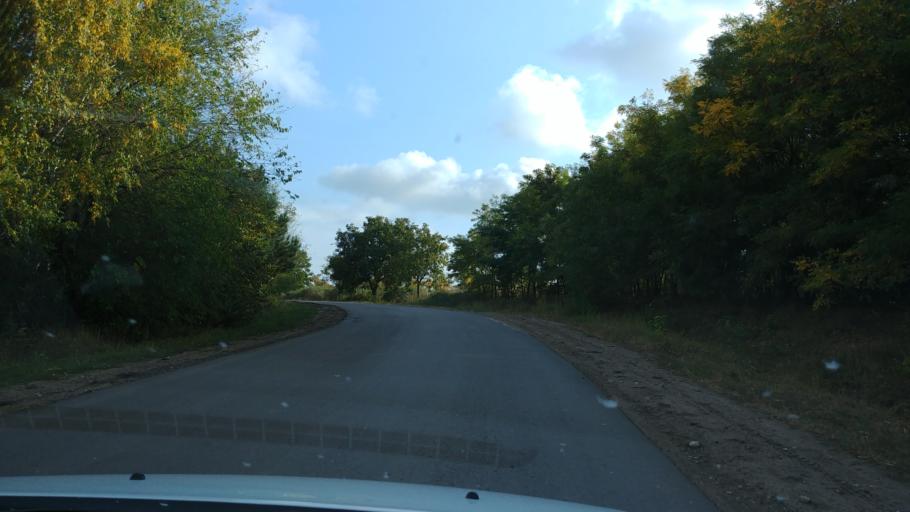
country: MD
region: Criuleni
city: Criuleni
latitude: 47.2159
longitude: 29.0669
